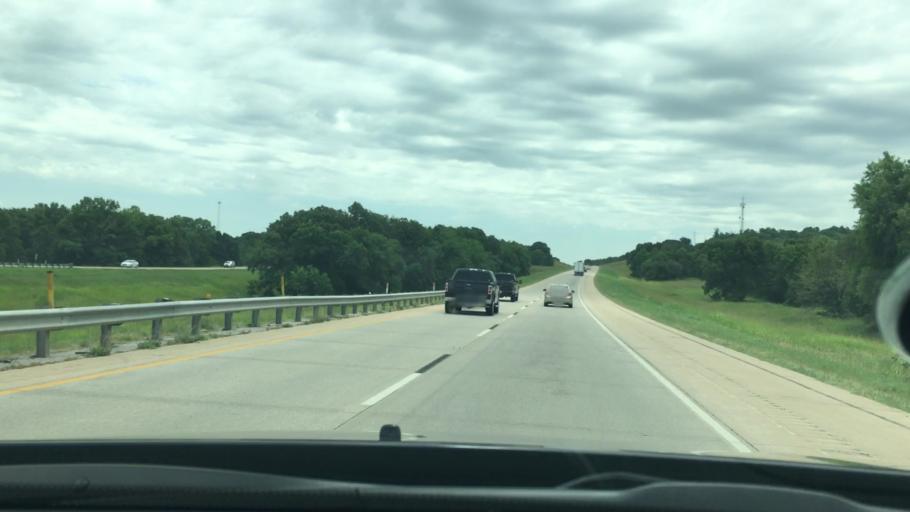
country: US
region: Oklahoma
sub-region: Love County
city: Marietta
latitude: 34.0091
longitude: -97.1432
